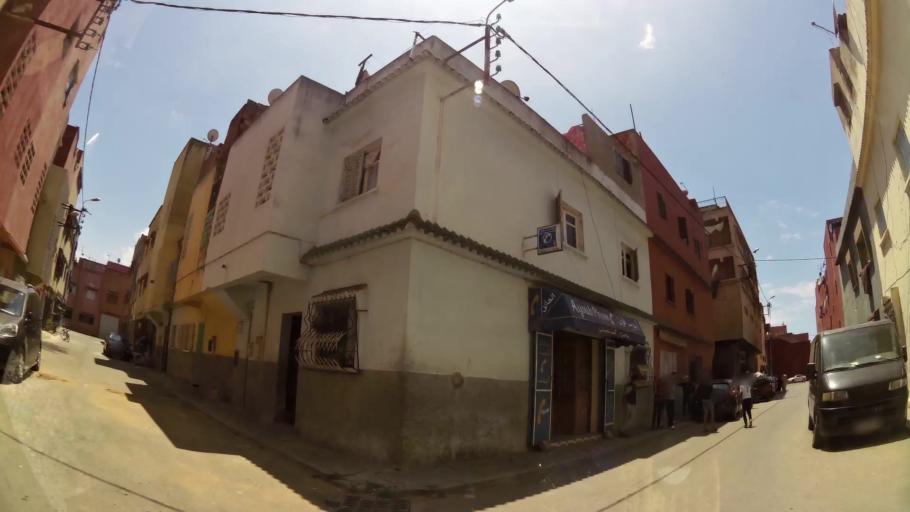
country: MA
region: Gharb-Chrarda-Beni Hssen
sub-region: Kenitra Province
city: Kenitra
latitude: 34.2653
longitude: -6.5546
